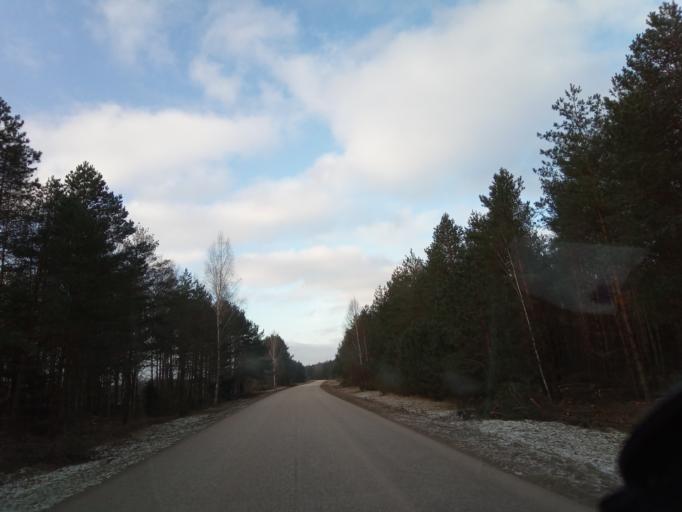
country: LT
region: Alytaus apskritis
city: Druskininkai
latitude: 53.9772
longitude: 24.2478
